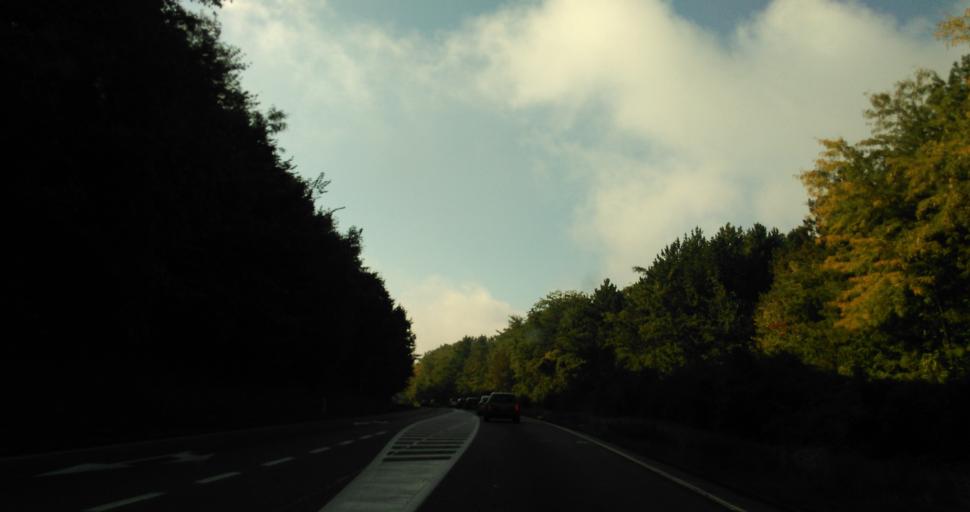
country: RS
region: Central Serbia
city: Sremcica
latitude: 44.6428
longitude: 20.4128
